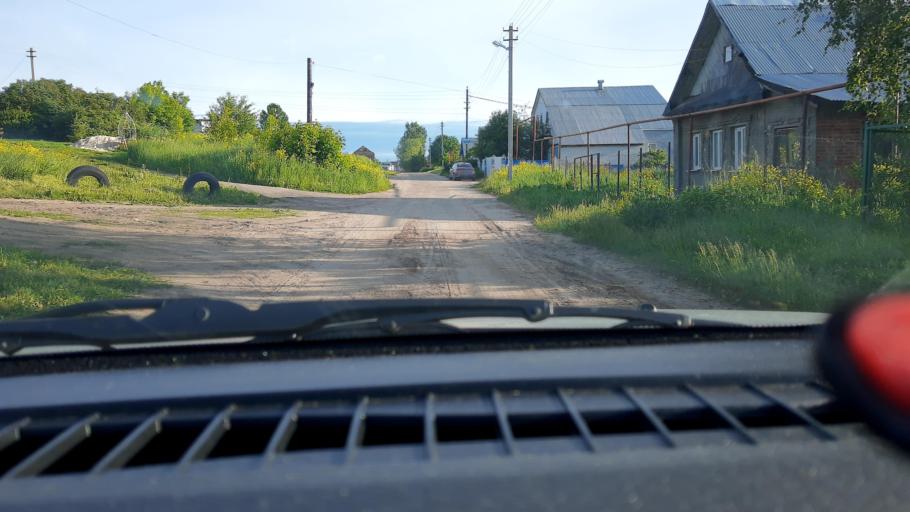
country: RU
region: Nizjnij Novgorod
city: Afonino
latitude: 56.1249
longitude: 44.0264
